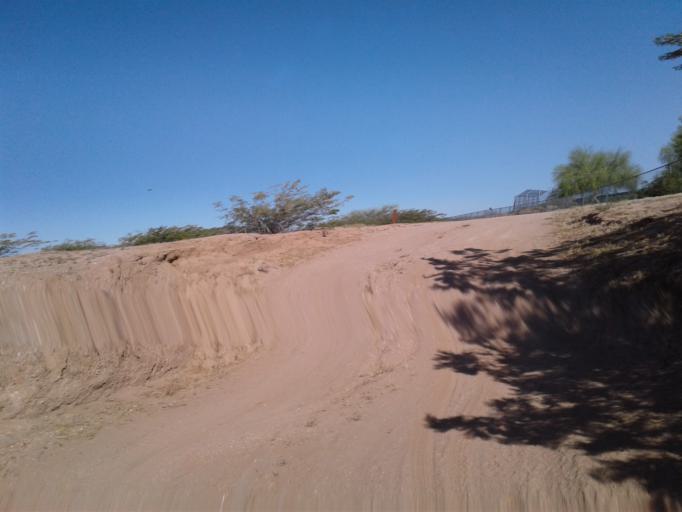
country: US
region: Arizona
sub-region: Maricopa County
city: Paradise Valley
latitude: 33.6779
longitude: -112.0092
